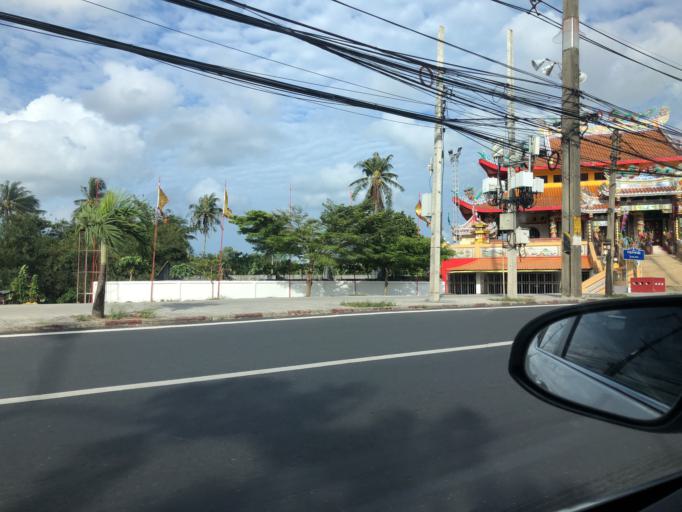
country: TH
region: Phuket
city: Ban Ko Kaeo
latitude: 7.9765
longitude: 98.3685
